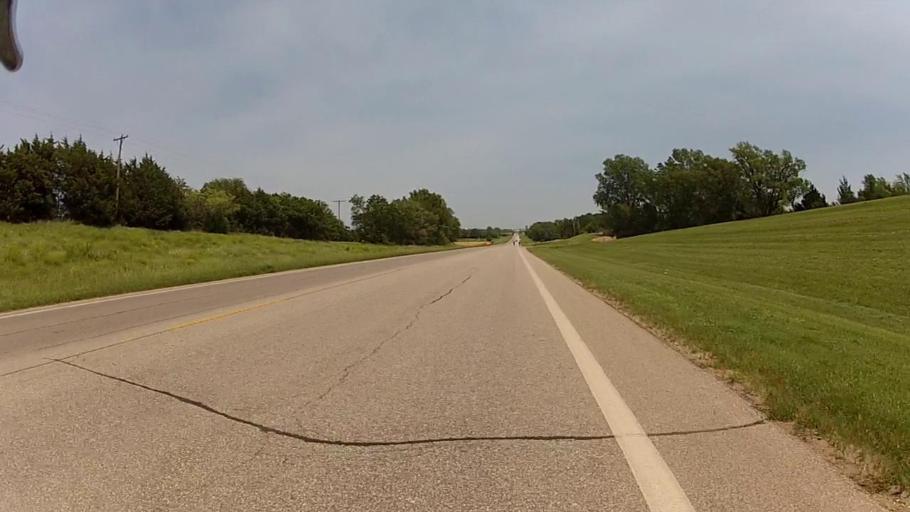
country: US
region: Kansas
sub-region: Cowley County
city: Arkansas City
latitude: 37.0565
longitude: -97.0721
